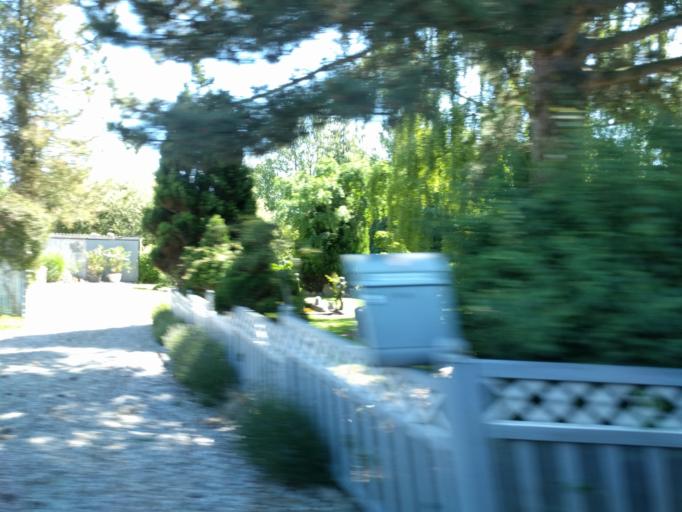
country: DK
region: South Denmark
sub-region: Kerteminde Kommune
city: Langeskov
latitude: 55.3471
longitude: 10.5820
